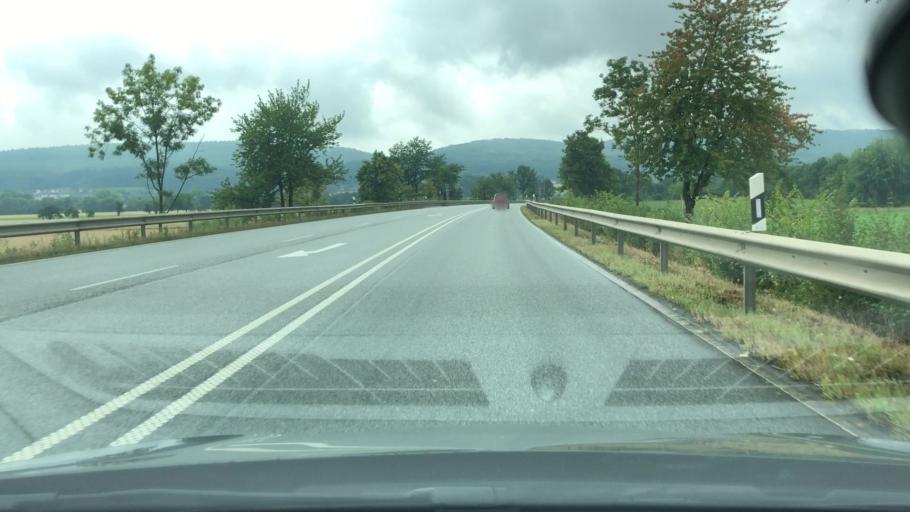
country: DE
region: North Rhine-Westphalia
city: Porta Westfalica
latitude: 52.2658
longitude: 8.9624
